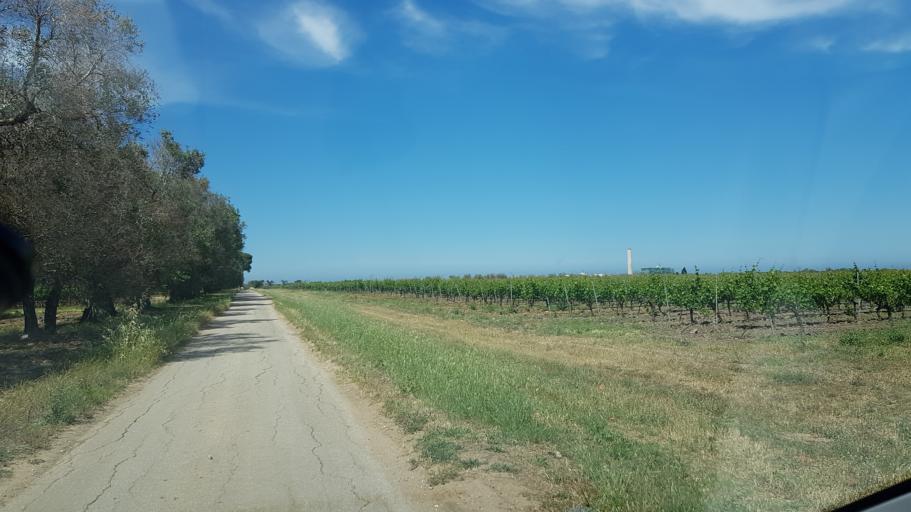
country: IT
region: Apulia
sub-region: Provincia di Brindisi
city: San Pietro Vernotico
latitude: 40.5360
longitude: 17.9962
